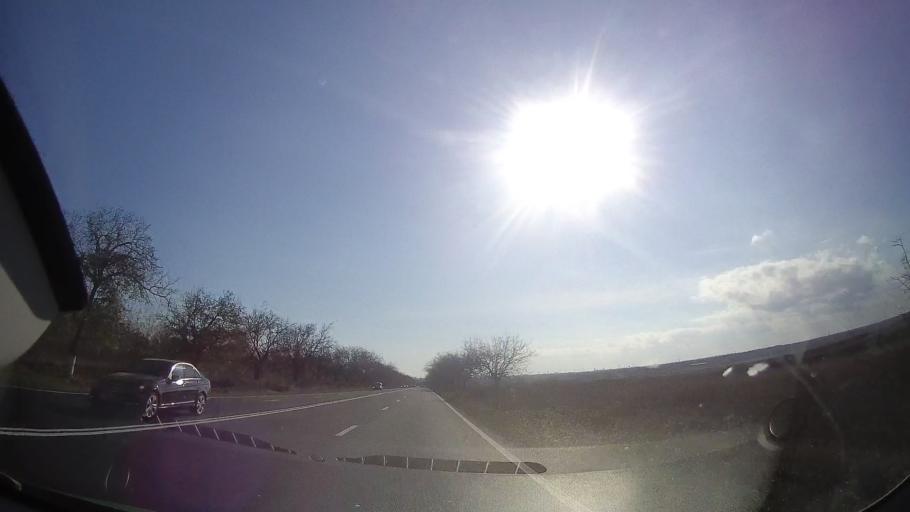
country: RO
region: Constanta
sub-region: Municipiul Mangalia
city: Mangalia
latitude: 43.8545
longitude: 28.5760
